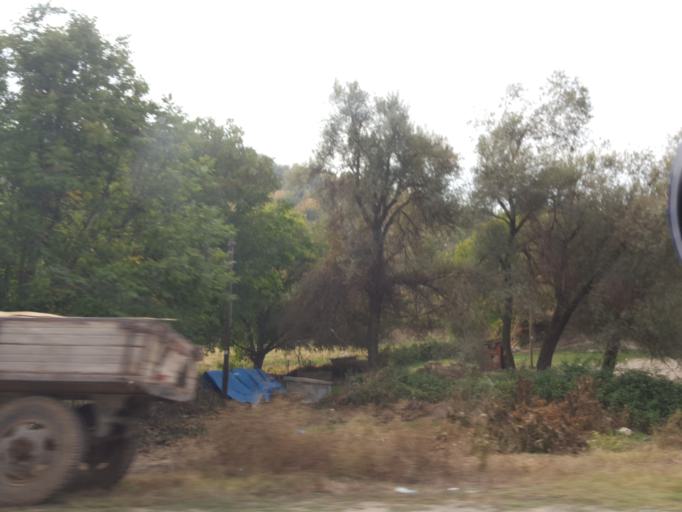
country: TR
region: Amasya
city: Gediksaray
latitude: 40.4878
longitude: 35.7834
